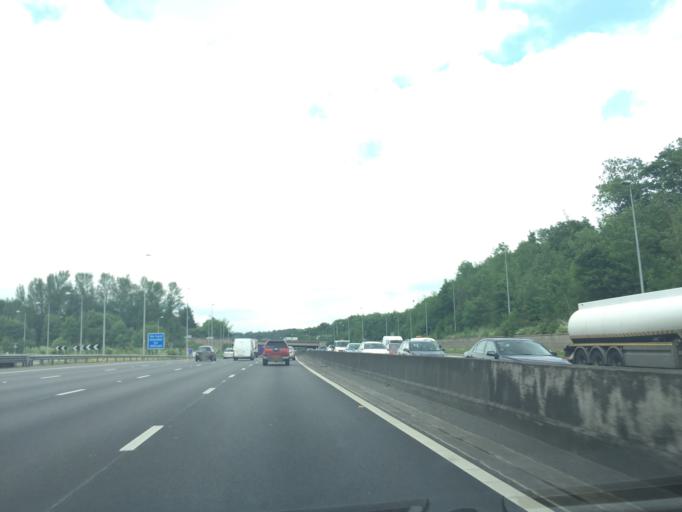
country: GB
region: England
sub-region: Hertfordshire
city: Chorleywood
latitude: 51.6528
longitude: -0.4971
